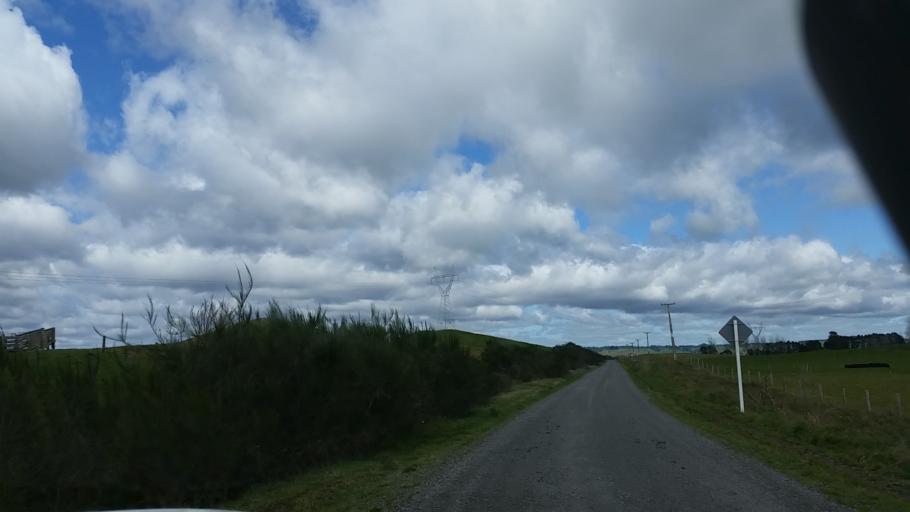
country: NZ
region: Bay of Plenty
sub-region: Whakatane District
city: Murupara
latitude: -38.2944
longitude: 176.5697
